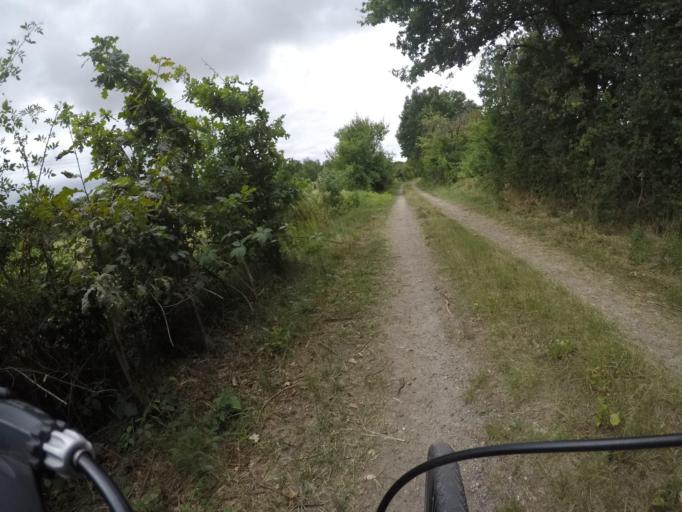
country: DE
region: Lower Saxony
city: Neu Darchau
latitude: 53.2809
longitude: 10.9101
